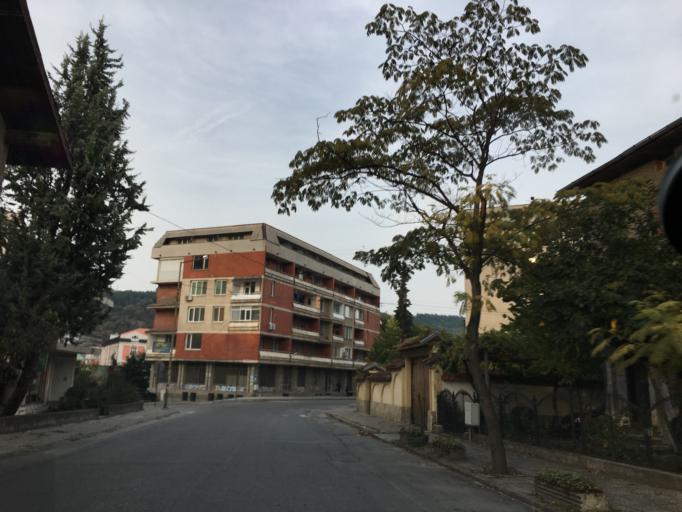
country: BG
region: Pazardzhik
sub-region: Obshtina Belovo
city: Belovo
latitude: 42.2130
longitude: 24.0155
